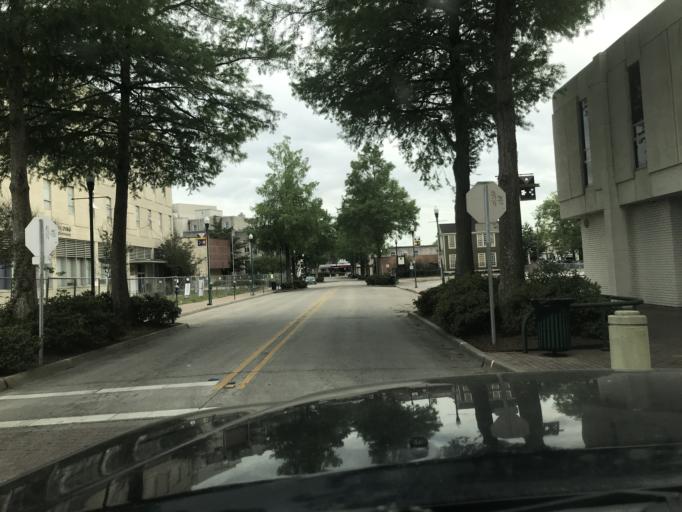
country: US
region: Louisiana
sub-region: Lafayette Parish
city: Lafayette
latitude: 30.2229
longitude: -92.0188
